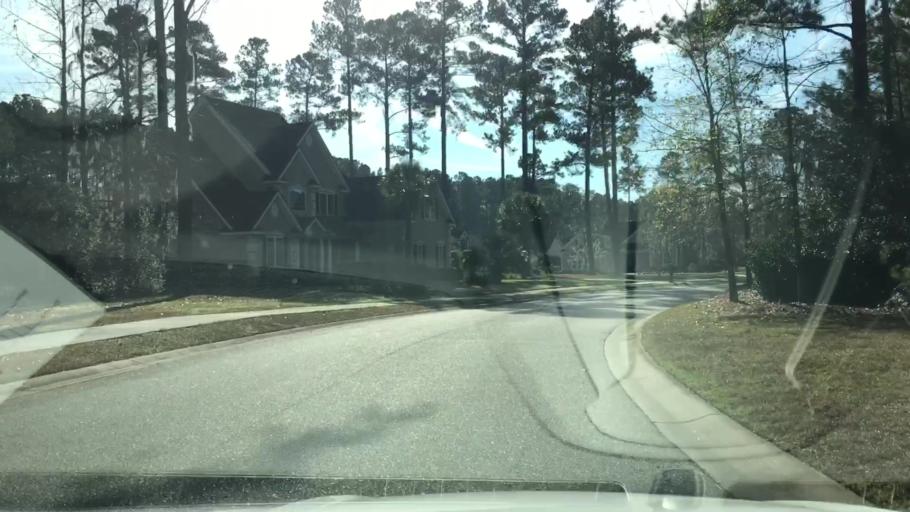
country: US
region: South Carolina
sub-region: Beaufort County
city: Bluffton
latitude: 32.2445
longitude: -80.9132
